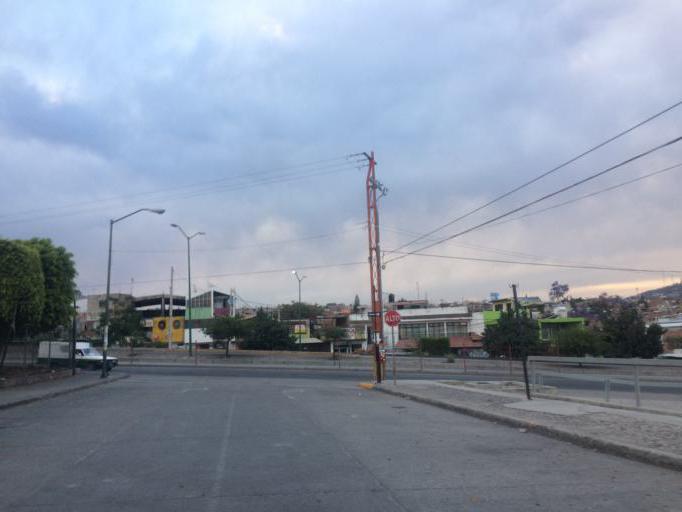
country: MX
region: Guanajuato
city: Leon
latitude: 21.1328
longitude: -101.6988
